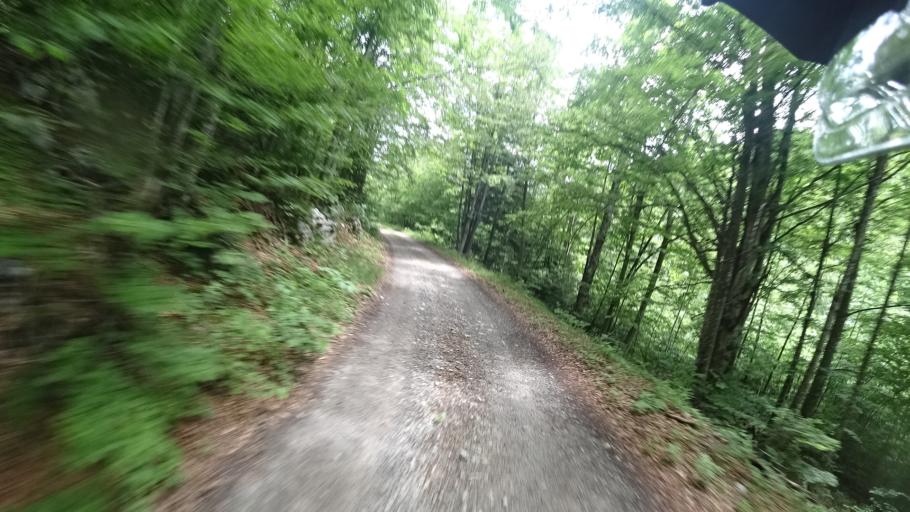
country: SI
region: Osilnica
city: Osilnica
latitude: 45.4949
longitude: 14.7337
